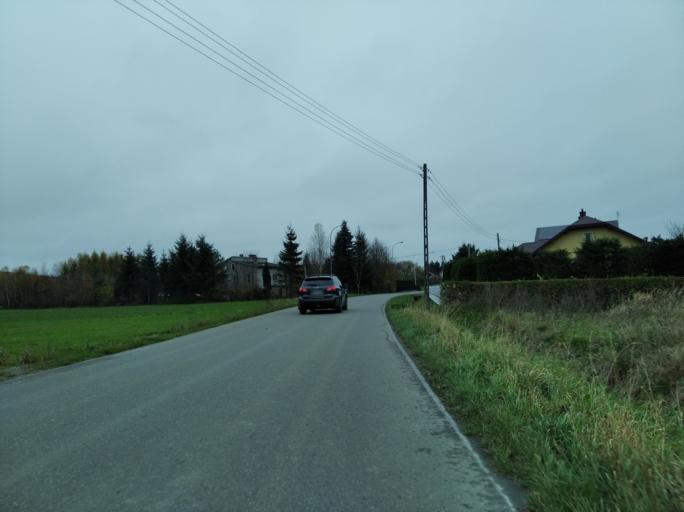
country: PL
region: Subcarpathian Voivodeship
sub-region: Powiat krosnienski
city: Chorkowka
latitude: 49.6833
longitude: 21.6734
